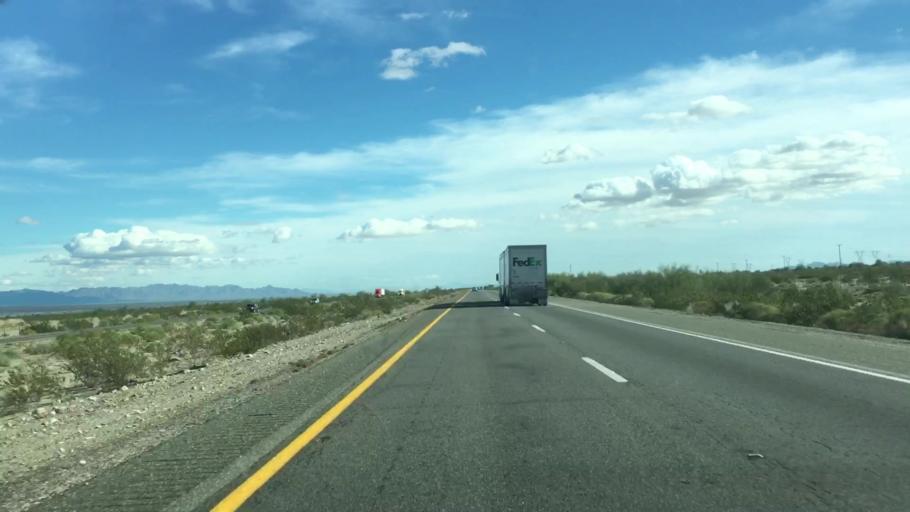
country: US
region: California
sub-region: Imperial County
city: Niland
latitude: 33.6901
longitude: -115.2697
